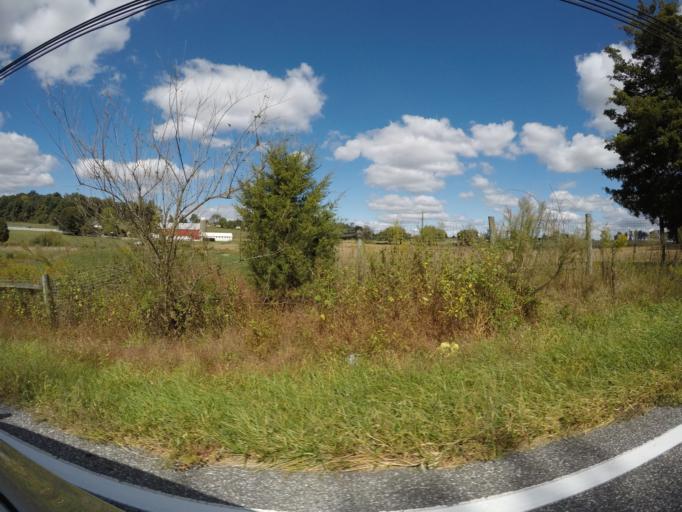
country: US
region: Maryland
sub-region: Harford County
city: Jarrettsville
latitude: 39.6972
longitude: -76.4483
